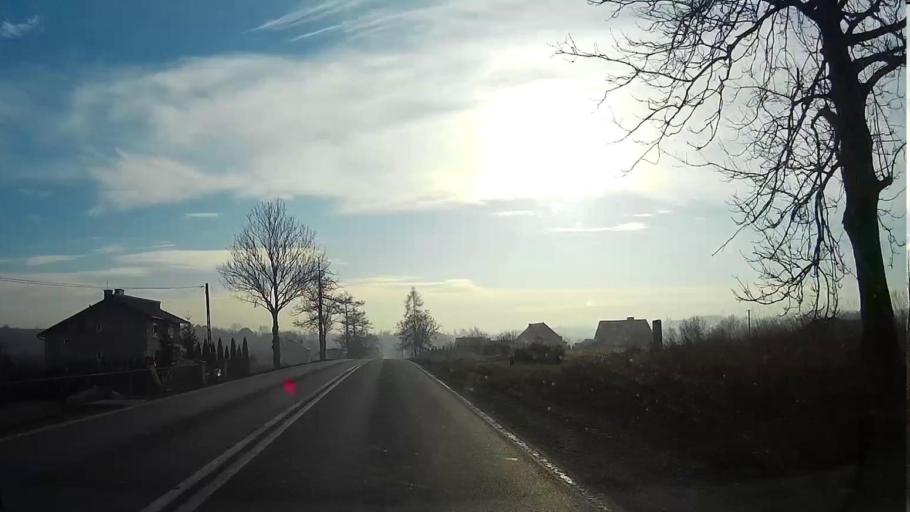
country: PL
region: Lesser Poland Voivodeship
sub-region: Powiat chrzanowski
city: Brodla
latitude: 50.0485
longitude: 19.5701
